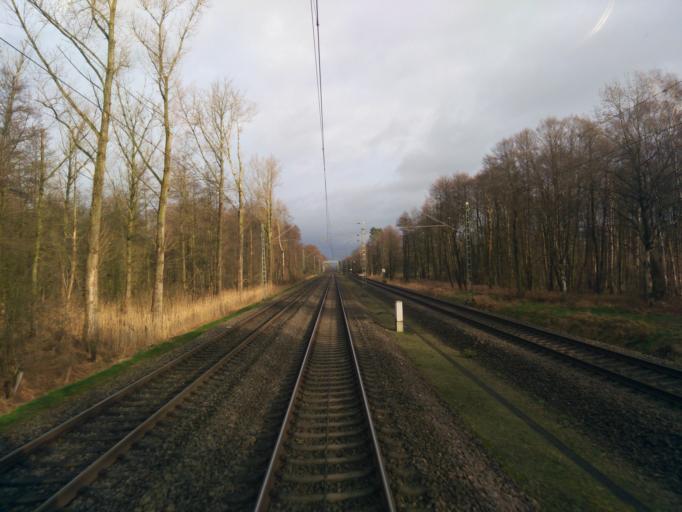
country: DE
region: Lower Saxony
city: Konigsmoor
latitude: 53.2465
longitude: 9.6767
